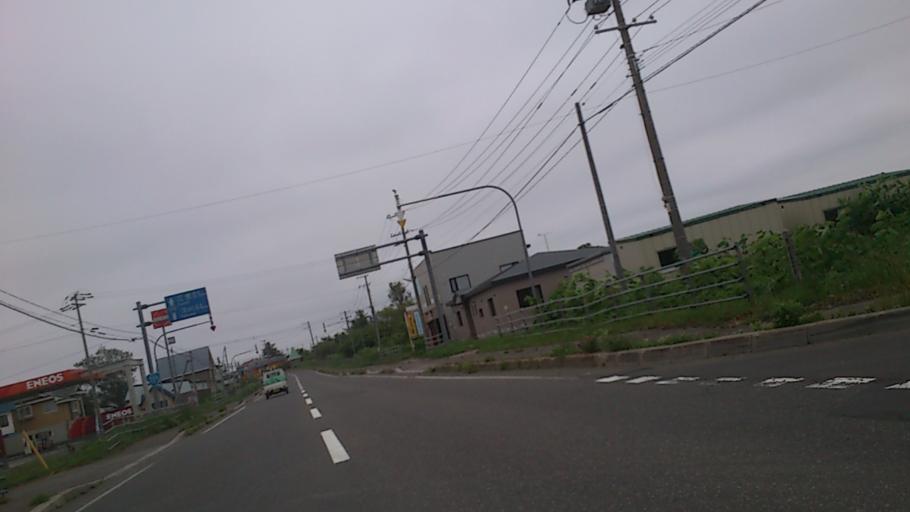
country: JP
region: Hokkaido
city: Iwanai
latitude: 42.4176
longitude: 139.8630
